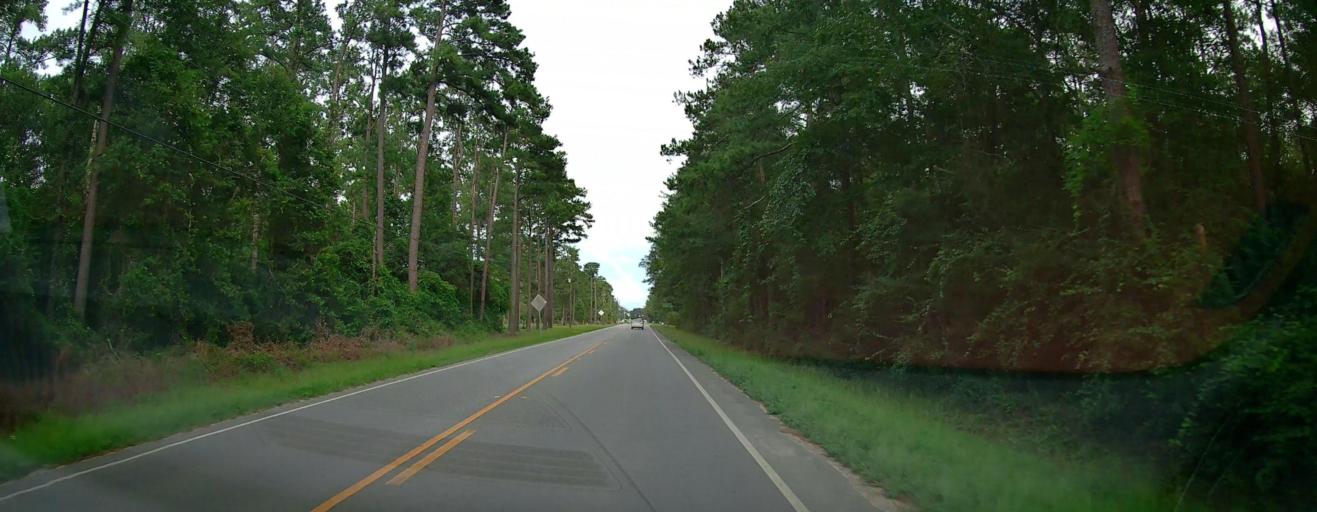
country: US
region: Georgia
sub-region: Wayne County
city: Jesup
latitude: 31.6628
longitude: -81.8563
